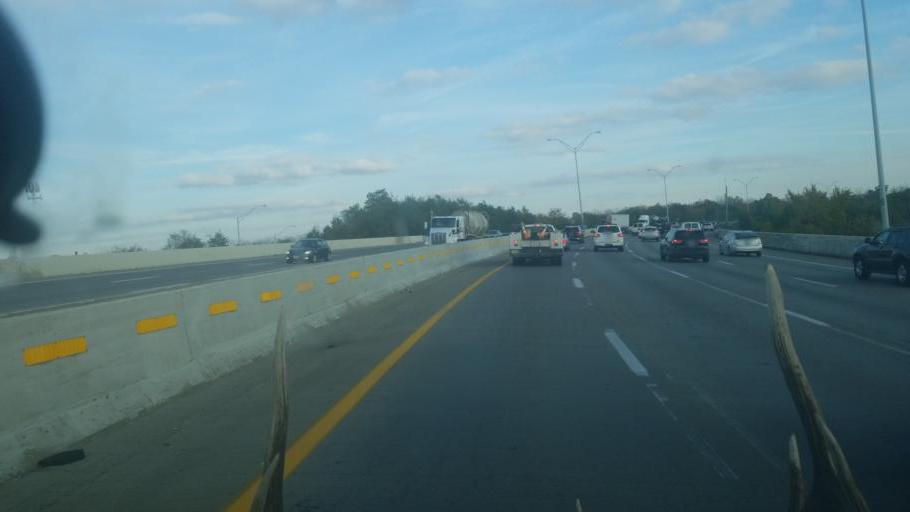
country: US
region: Ohio
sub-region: Franklin County
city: Bexley
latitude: 39.9528
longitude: -82.9475
